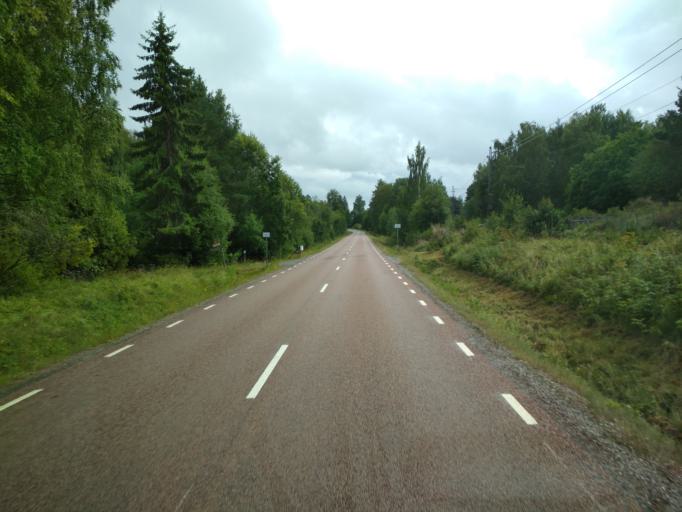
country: SE
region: Vaestmanland
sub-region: Surahammars Kommun
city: Ramnas
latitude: 59.7994
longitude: 16.1729
